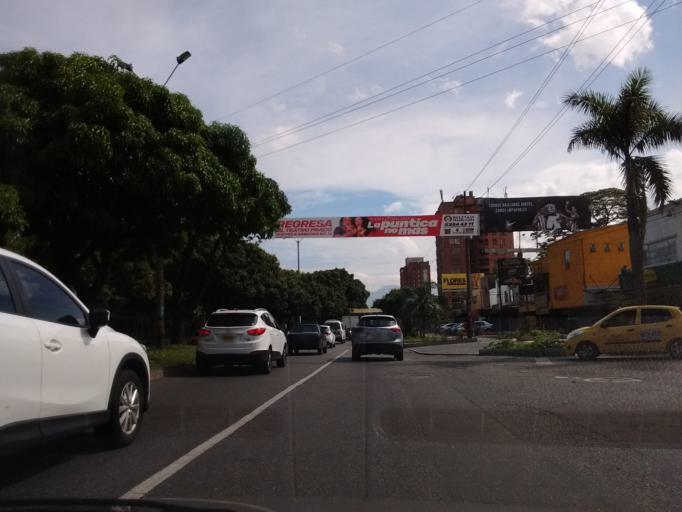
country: CO
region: Antioquia
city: Itagui
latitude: 6.2075
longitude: -75.5767
